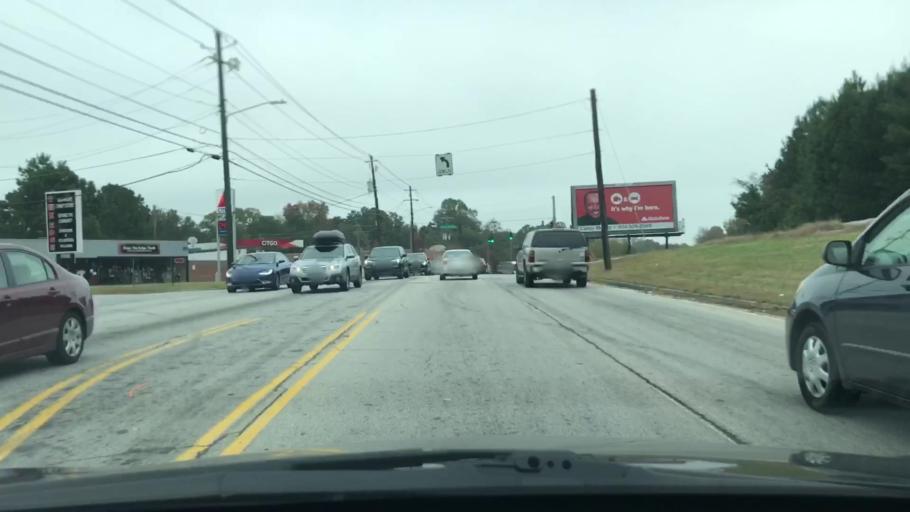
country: US
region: Georgia
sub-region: DeKalb County
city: Scottdale
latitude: 33.7941
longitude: -84.2636
